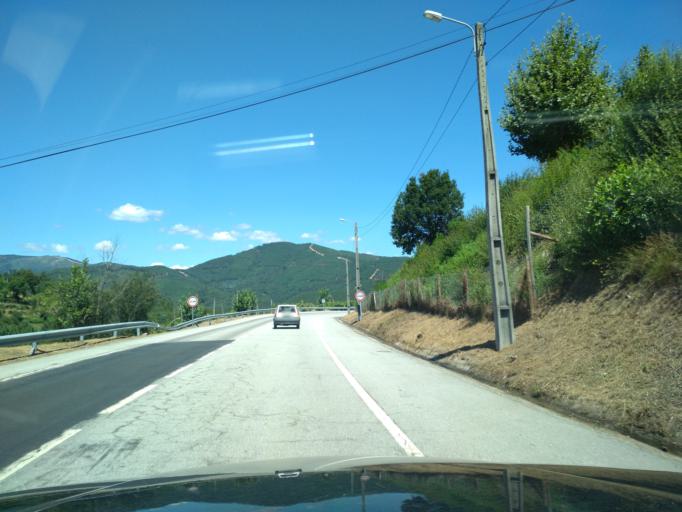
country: PT
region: Vila Real
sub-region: Ribeira de Pena
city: Sobreira
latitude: 41.5242
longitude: -7.7860
